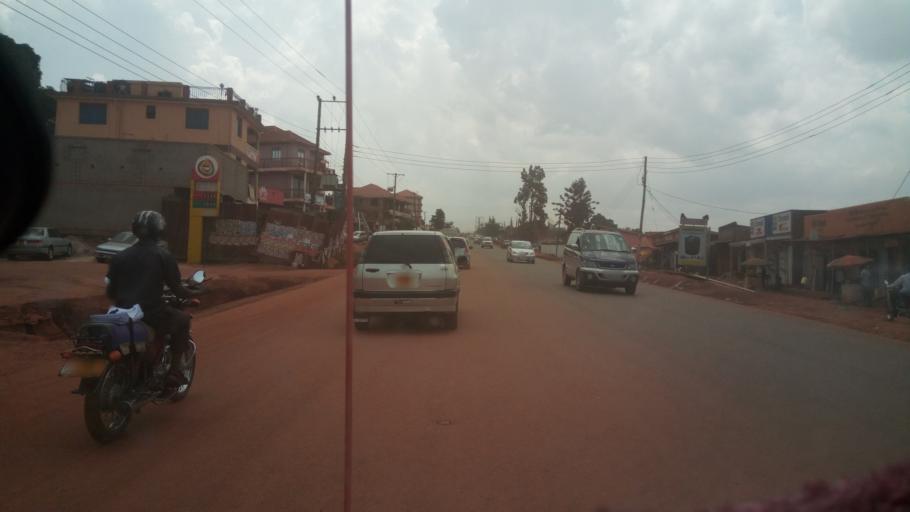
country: UG
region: Central Region
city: Kampala Central Division
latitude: 0.3512
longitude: 32.5380
